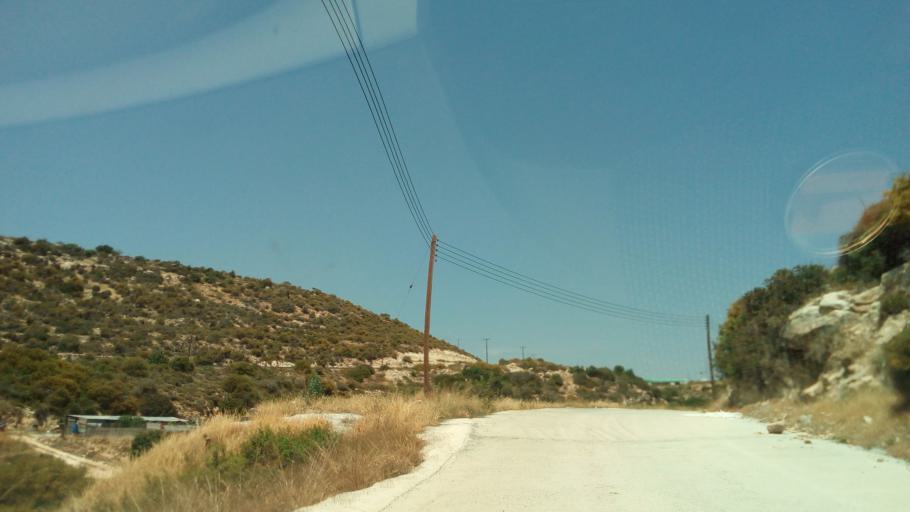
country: CY
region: Limassol
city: Ypsonas
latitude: 34.7165
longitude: 32.9536
